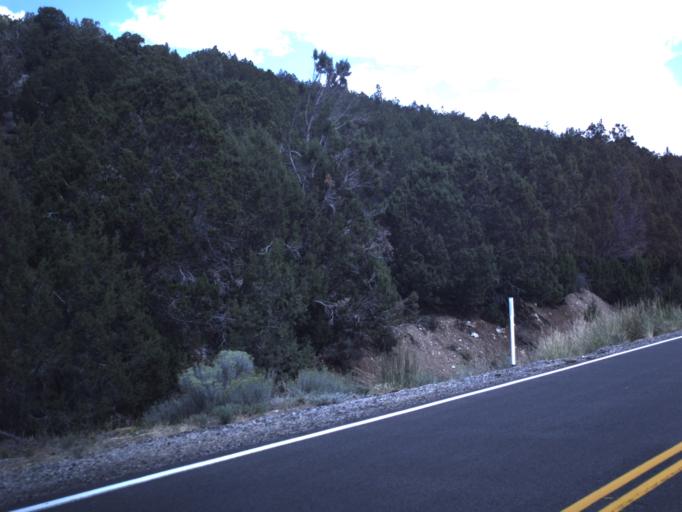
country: US
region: Utah
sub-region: Tooele County
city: Grantsville
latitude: 40.3423
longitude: -112.5801
